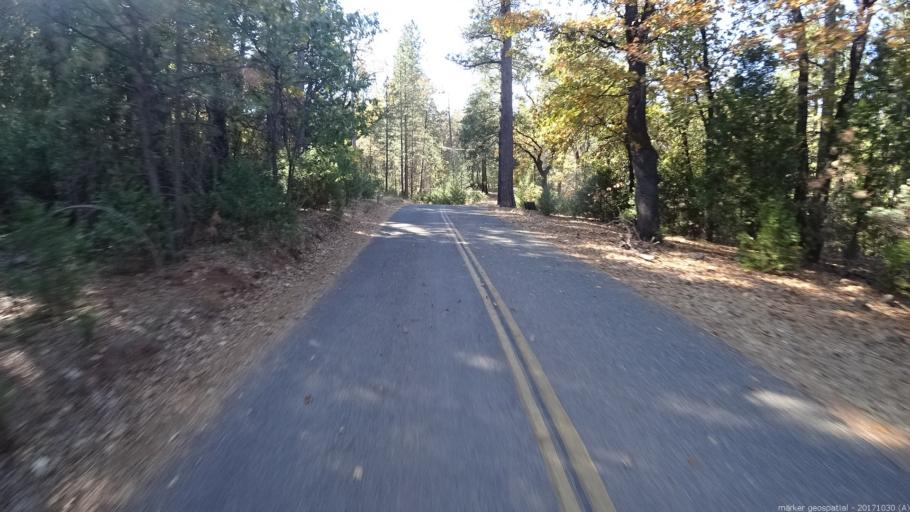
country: US
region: California
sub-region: Shasta County
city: Shingletown
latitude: 40.6030
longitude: -121.9583
